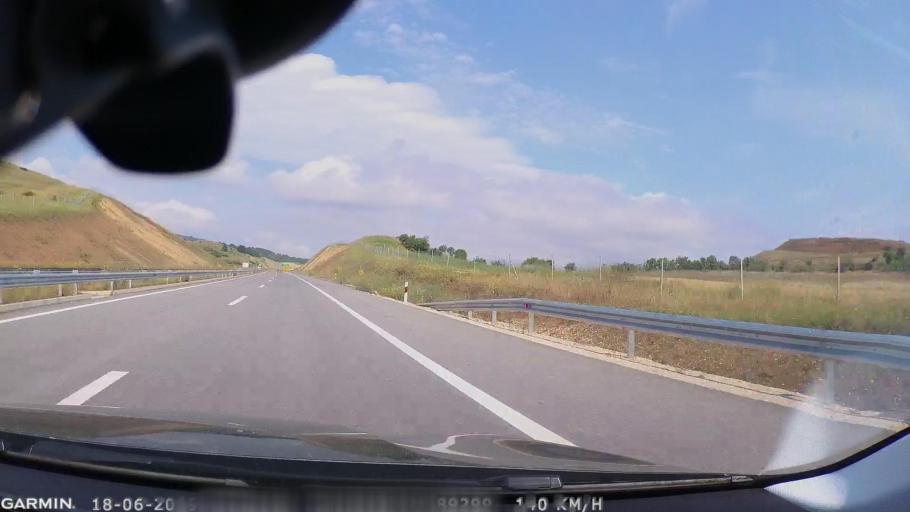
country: MK
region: Sveti Nikole
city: Gorobinci
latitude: 41.9130
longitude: 21.8940
